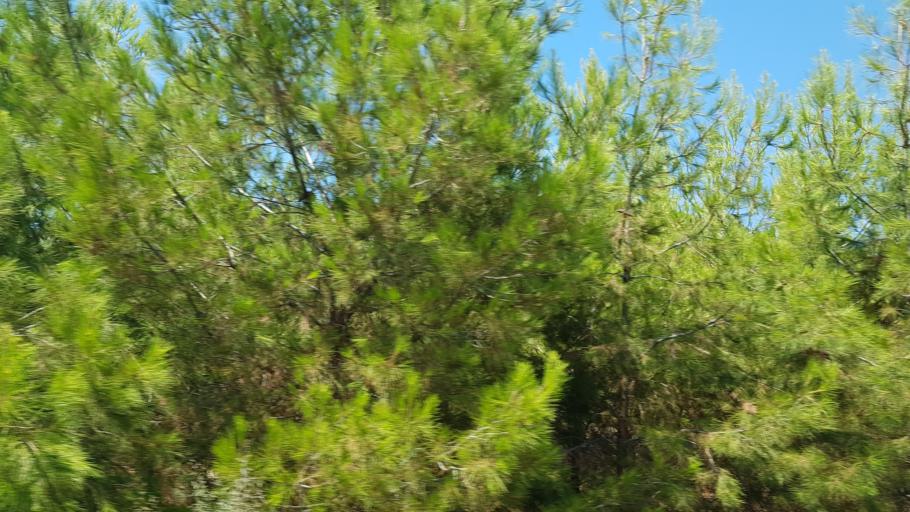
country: TR
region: Mugla
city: Karaova
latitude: 37.0410
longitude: 27.7291
